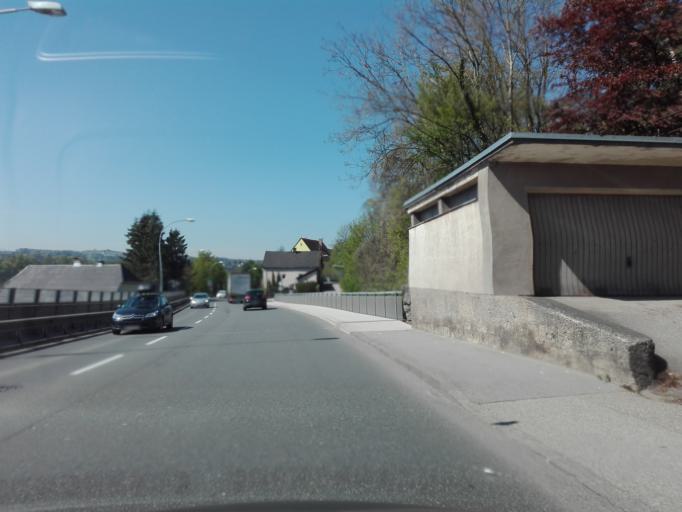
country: AT
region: Upper Austria
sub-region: Steyr Stadt
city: Steyr
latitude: 48.0453
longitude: 14.4086
